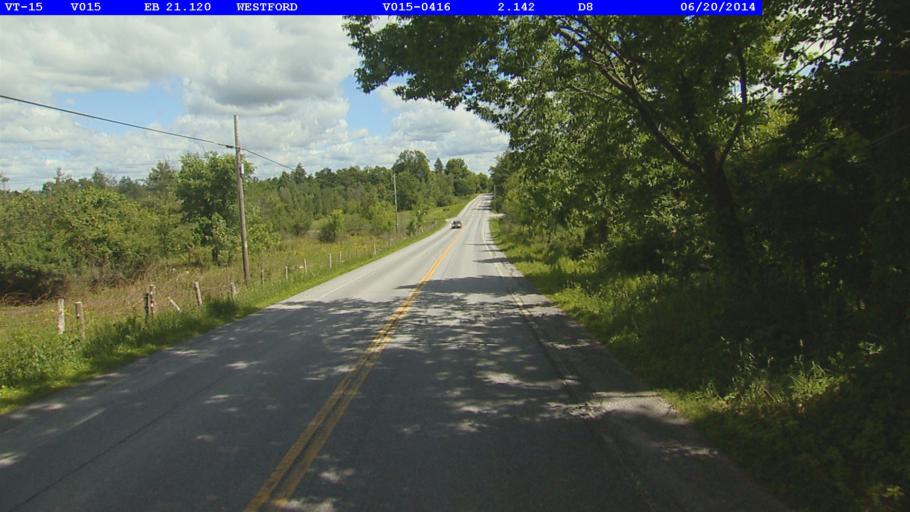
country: US
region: Vermont
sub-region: Chittenden County
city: Jericho
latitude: 44.6237
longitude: -72.9234
